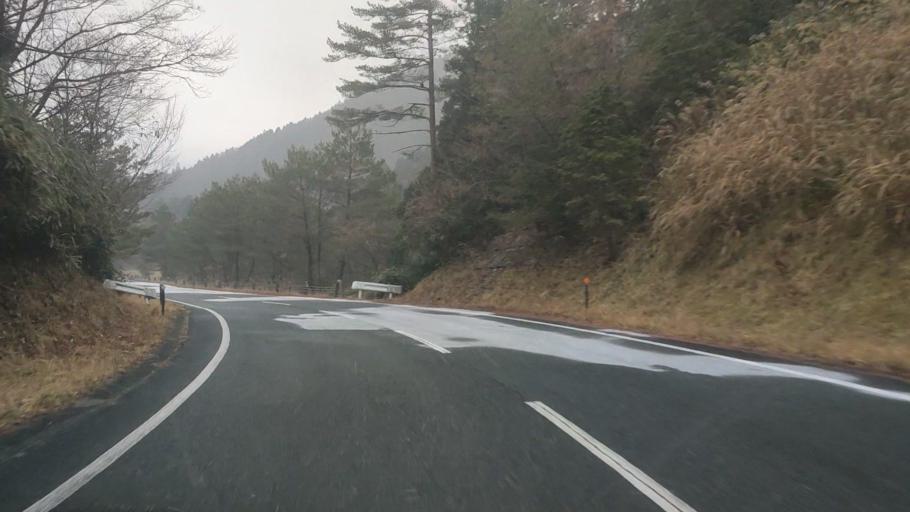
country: JP
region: Kumamoto
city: Matsubase
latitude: 32.5671
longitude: 130.9096
